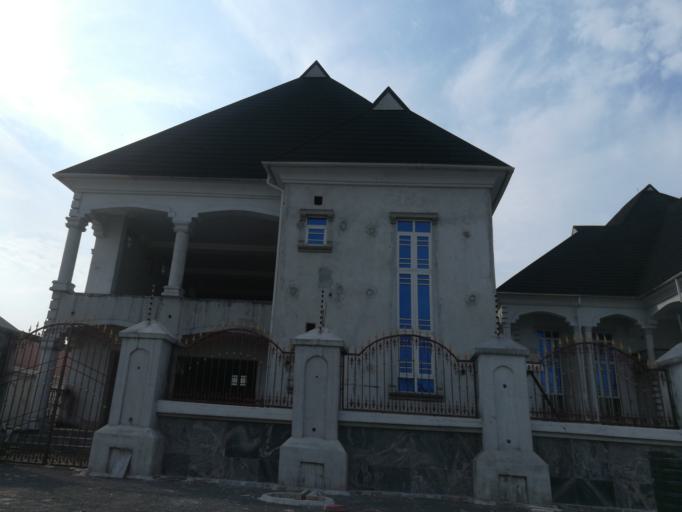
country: NG
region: Rivers
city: Okrika
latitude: 4.7314
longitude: 7.0828
